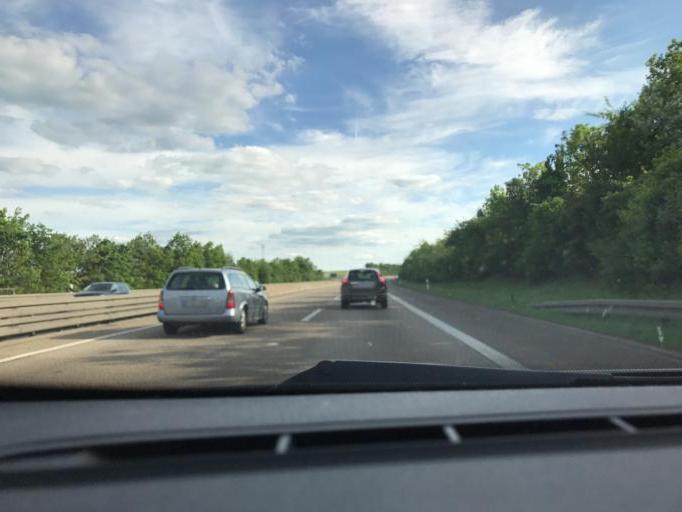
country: DE
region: North Rhine-Westphalia
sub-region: Regierungsbezirk Koln
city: Mechernich
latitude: 50.6197
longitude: 6.7161
